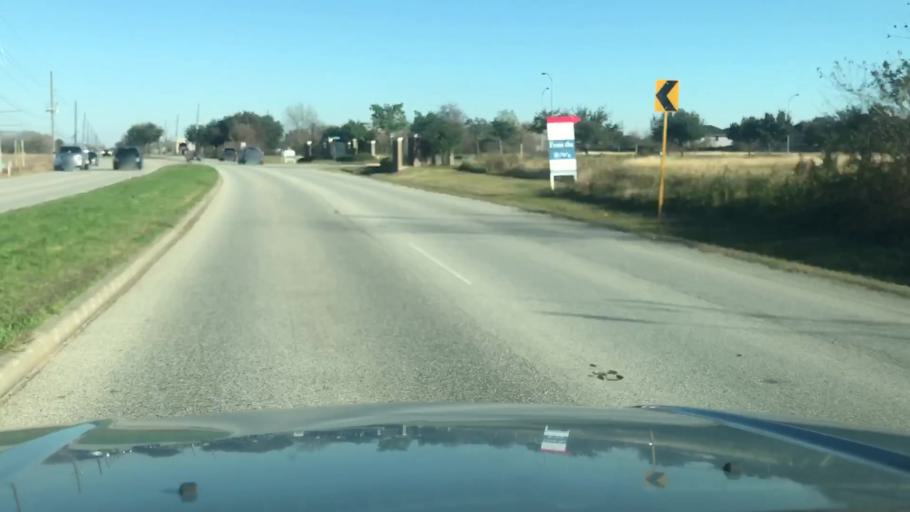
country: US
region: Texas
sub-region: Fort Bend County
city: Cinco Ranch
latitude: 29.8313
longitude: -95.7382
